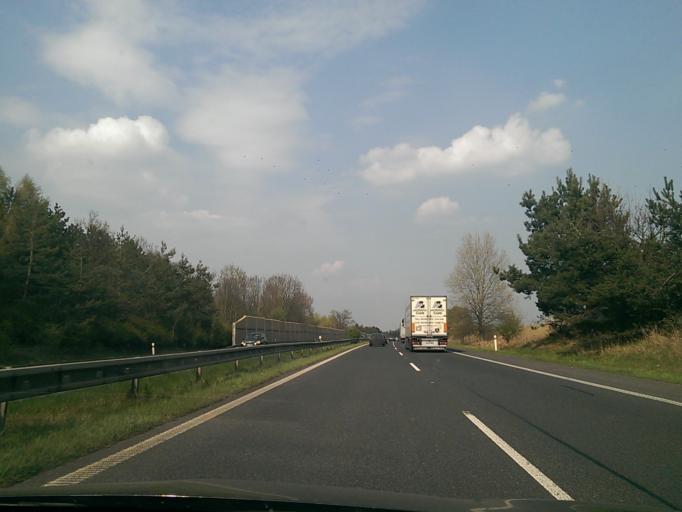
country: CZ
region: Central Bohemia
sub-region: Okres Mlada Boleslav
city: Mlada Boleslav
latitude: 50.3620
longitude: 14.8755
